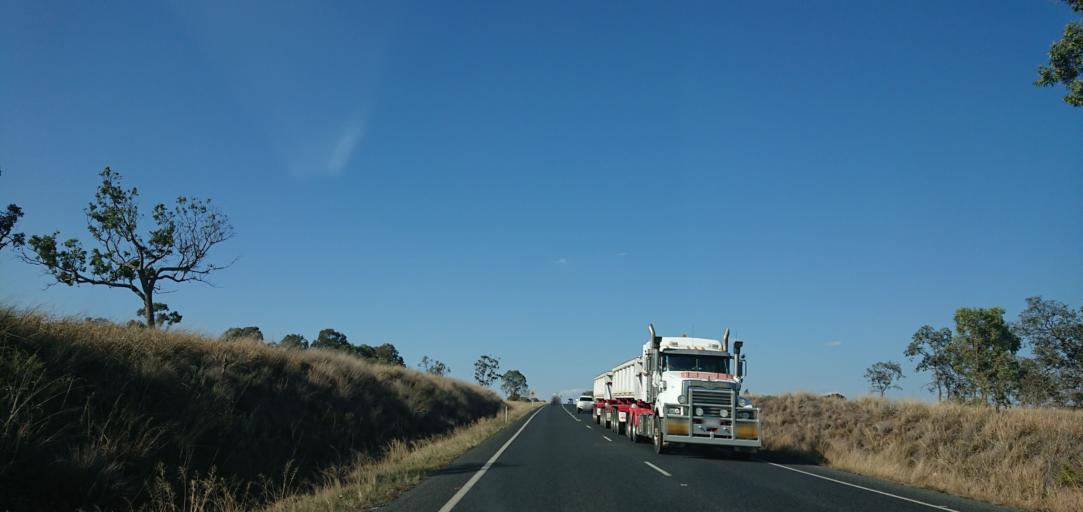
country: AU
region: Queensland
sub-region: Toowoomba
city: Westbrook
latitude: -27.6465
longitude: 151.7287
